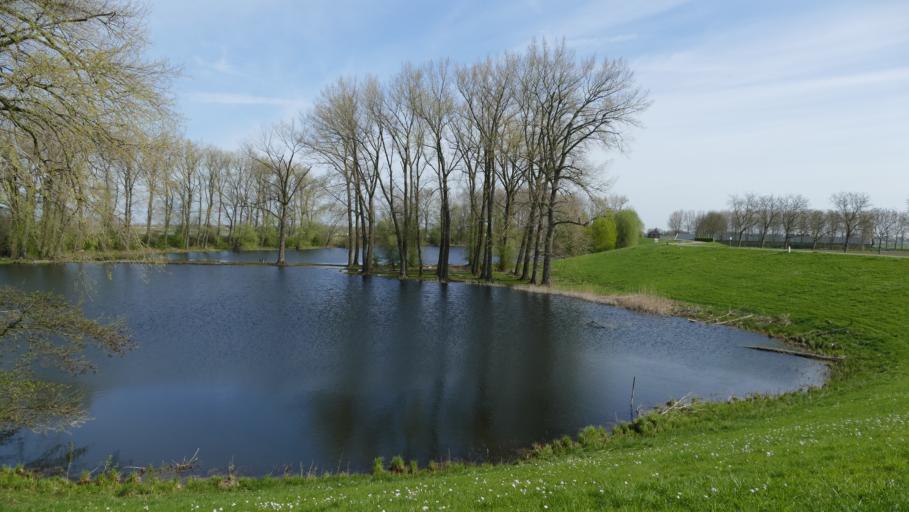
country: NL
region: North Brabant
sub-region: Gemeente 's-Hertogenbosch
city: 's-Hertogenbosch
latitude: 51.7424
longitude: 5.3395
